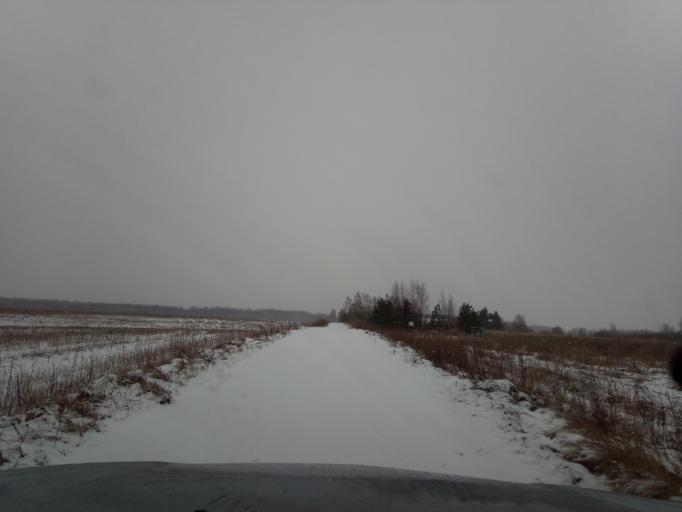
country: LT
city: Ramygala
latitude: 55.5881
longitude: 24.3627
